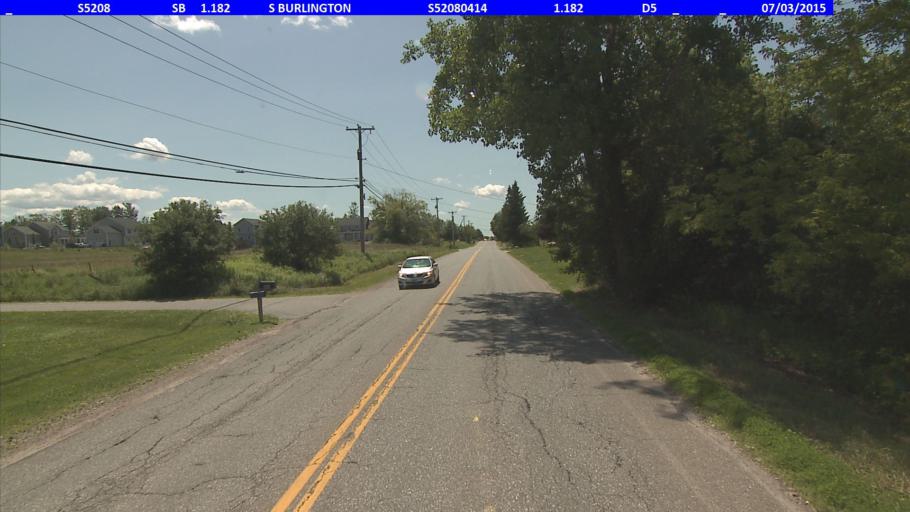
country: US
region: Vermont
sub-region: Chittenden County
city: South Burlington
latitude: 44.4278
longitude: -73.1746
